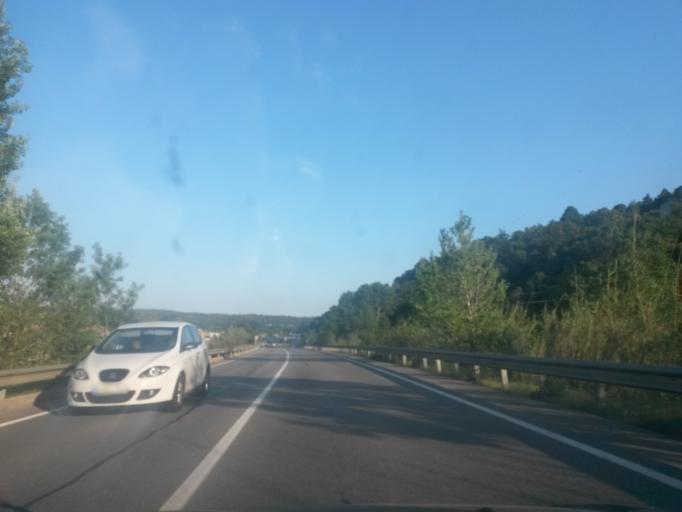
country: ES
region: Catalonia
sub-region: Provincia de Girona
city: Besalu
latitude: 42.1937
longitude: 2.7268
